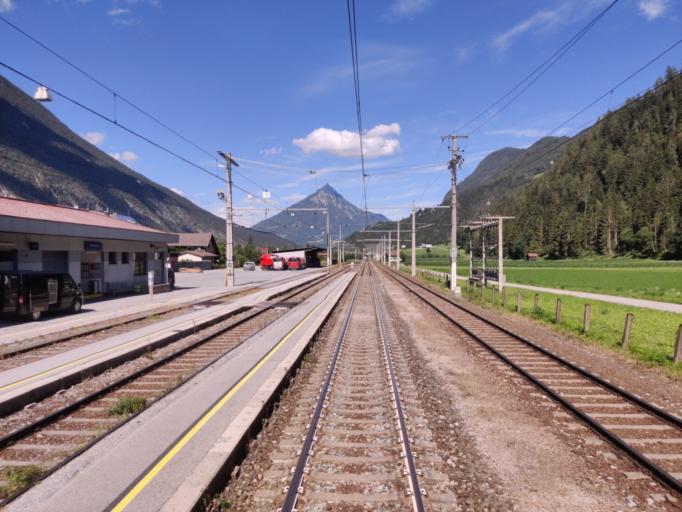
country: AT
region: Tyrol
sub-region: Politischer Bezirk Landeck
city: Schonwies
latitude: 47.1972
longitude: 10.6605
